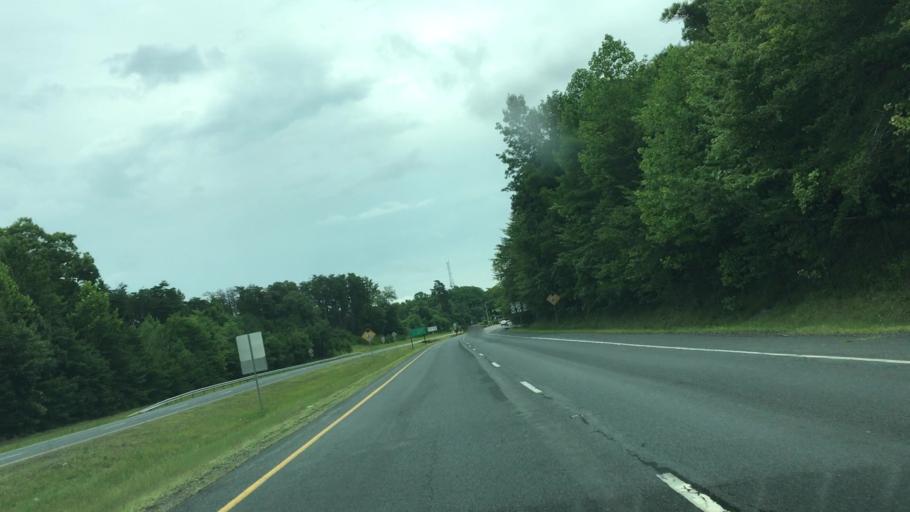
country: US
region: Virginia
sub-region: Prince William County
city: Lake Ridge
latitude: 38.6824
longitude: -77.3653
